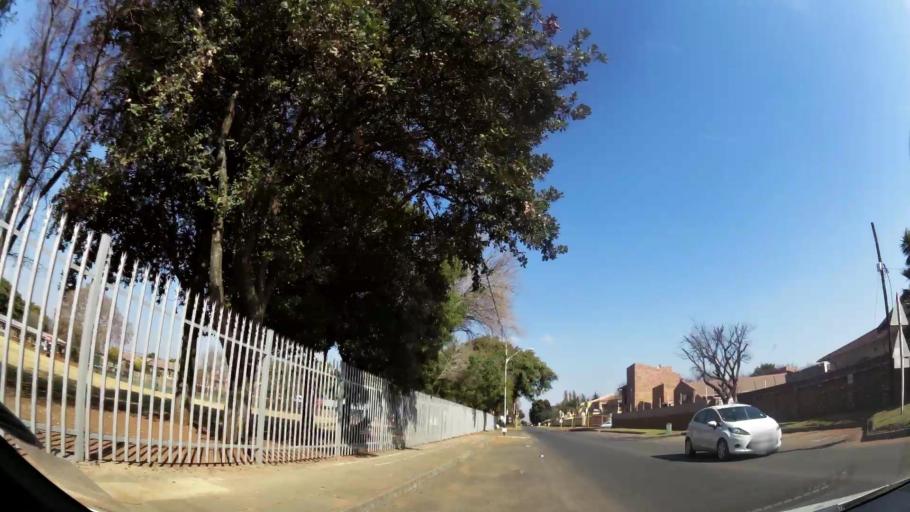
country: ZA
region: Gauteng
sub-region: Ekurhuleni Metropolitan Municipality
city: Boksburg
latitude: -26.1838
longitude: 28.2763
